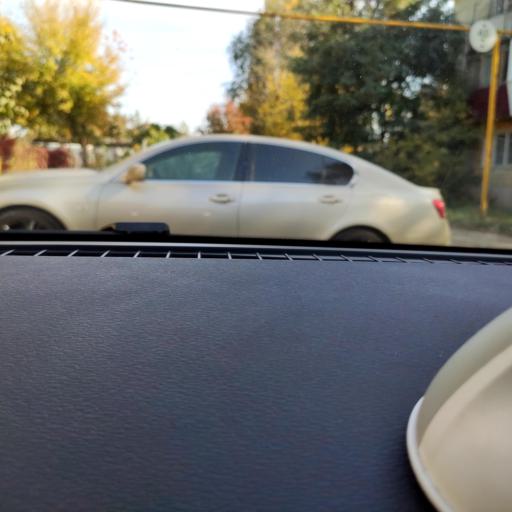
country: RU
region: Samara
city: Smyshlyayevka
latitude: 53.2021
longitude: 50.2877
